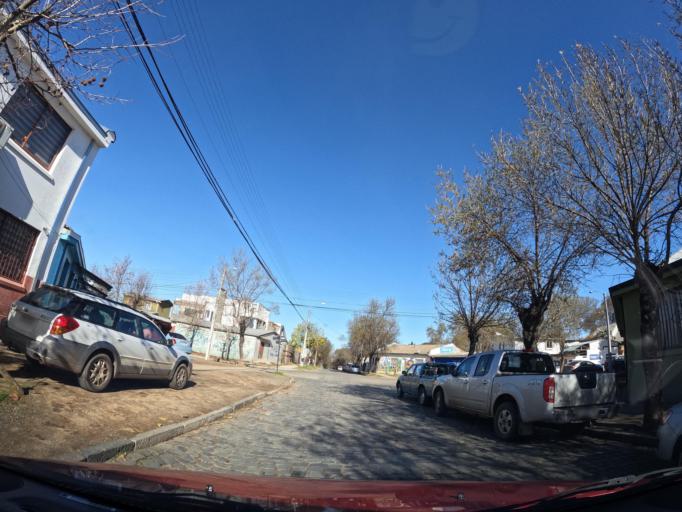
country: CL
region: Maule
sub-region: Provincia de Cauquenes
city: Cauquenes
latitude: -35.9710
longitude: -72.3164
